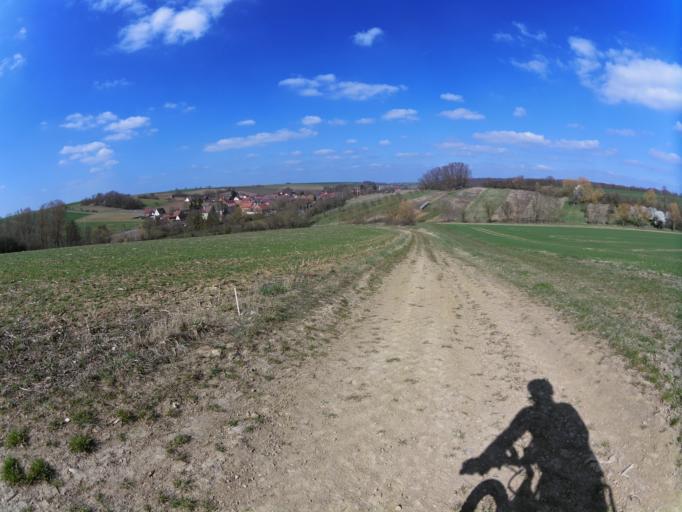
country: DE
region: Bavaria
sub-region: Regierungsbezirk Unterfranken
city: Prosselsheim
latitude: 49.8366
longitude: 10.1515
